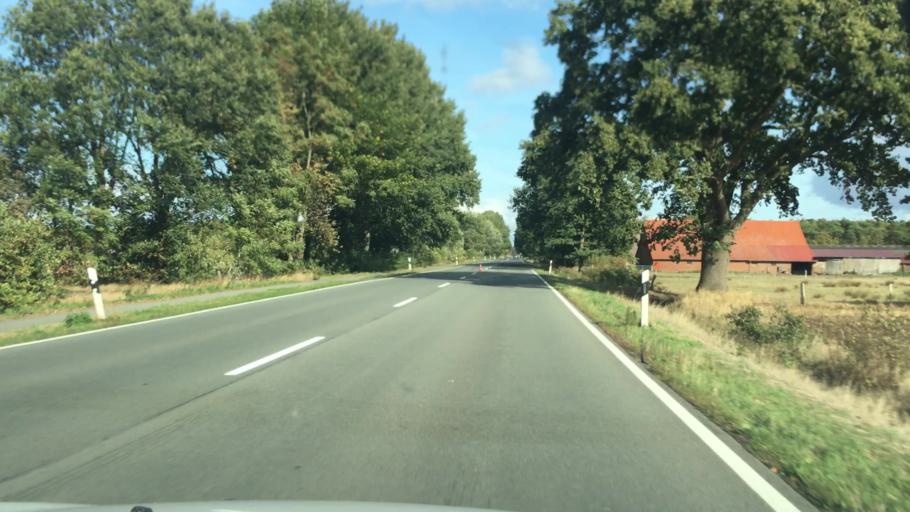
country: DE
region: Lower Saxony
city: Freistatt
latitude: 52.6167
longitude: 8.6383
